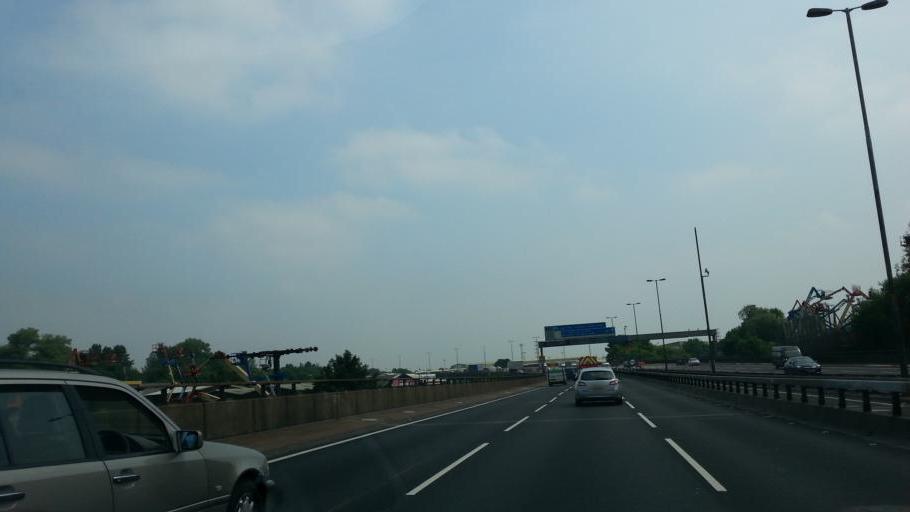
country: GB
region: England
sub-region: Sandwell
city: West Bromwich
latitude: 52.5063
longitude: -1.9866
